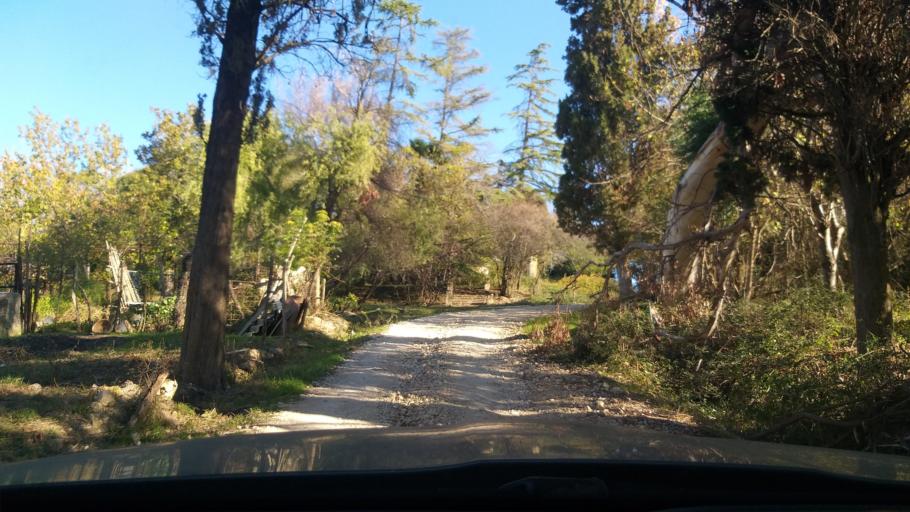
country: GE
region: Abkhazia
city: Stantsiya Novyy Afon
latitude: 43.0490
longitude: 40.8995
